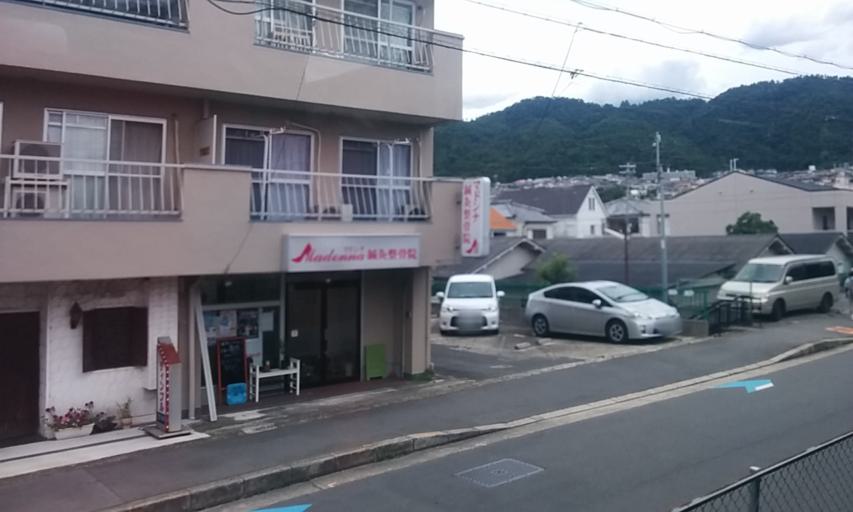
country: JP
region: Osaka
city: Mino
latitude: 34.8297
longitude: 135.4670
